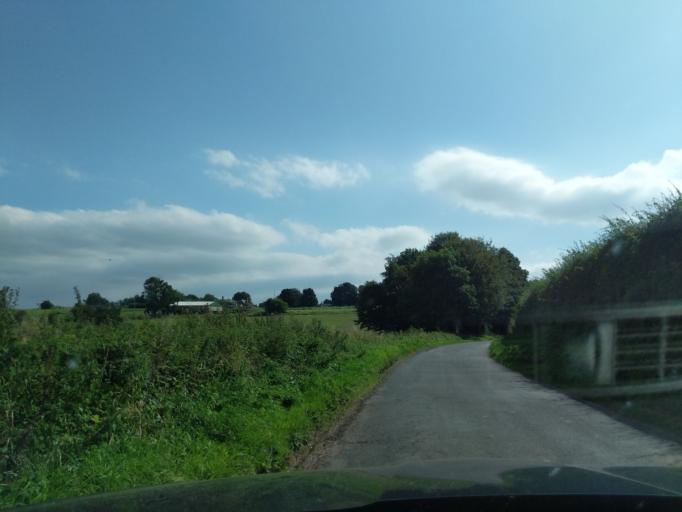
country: GB
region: England
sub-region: Northumberland
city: Ford
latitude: 55.6406
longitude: -2.1371
